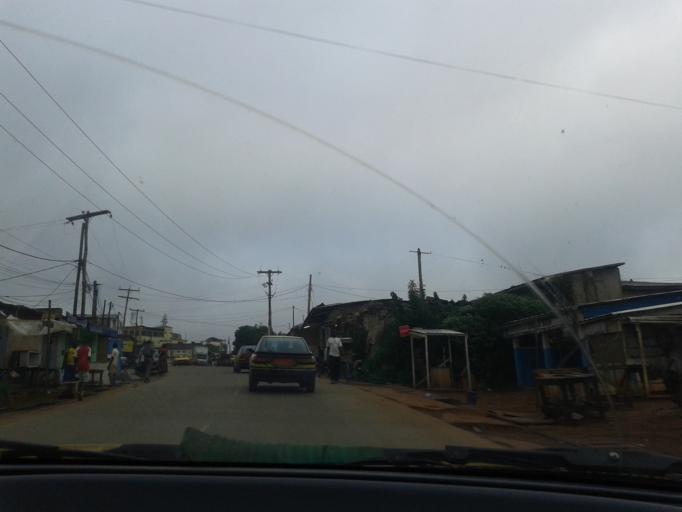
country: CM
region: Centre
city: Yaounde
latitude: 3.8840
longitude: 11.5263
